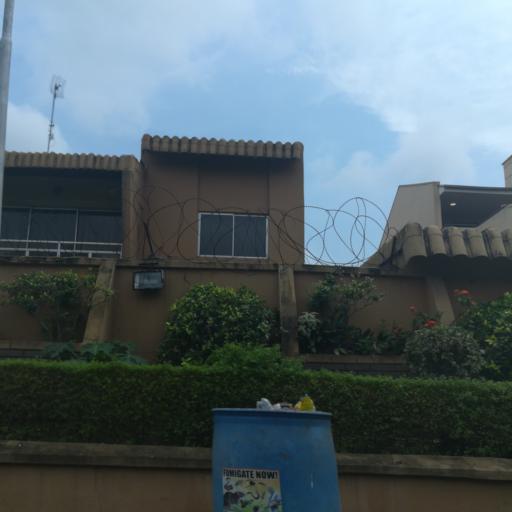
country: NG
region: Lagos
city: Ojota
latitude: 6.5759
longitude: 3.3933
